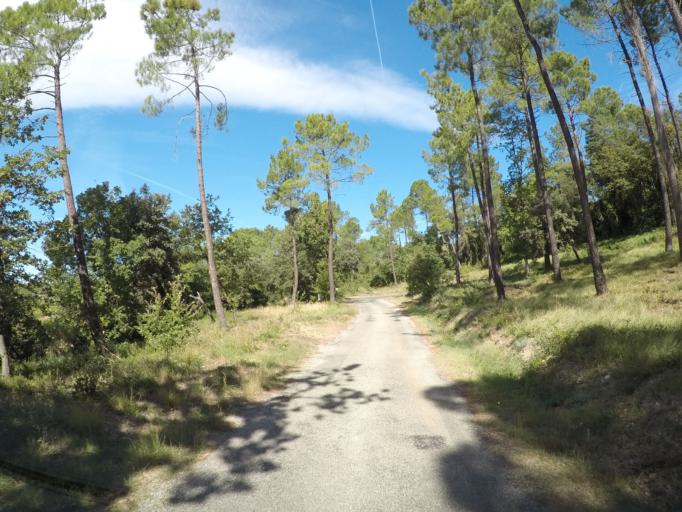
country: FR
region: Provence-Alpes-Cote d'Azur
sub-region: Departement du Vaucluse
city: Bollene
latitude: 44.2887
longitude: 4.7914
